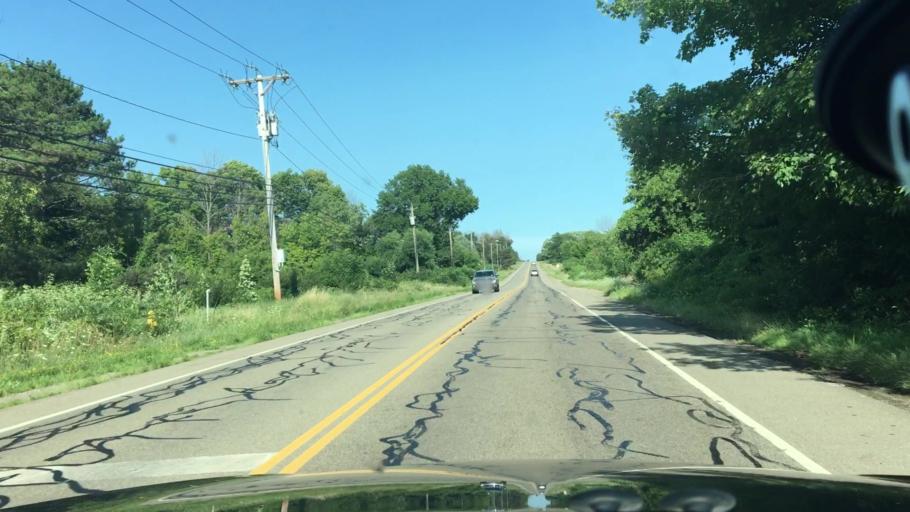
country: US
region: New York
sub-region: Erie County
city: Angola
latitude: 42.6525
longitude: -79.0082
